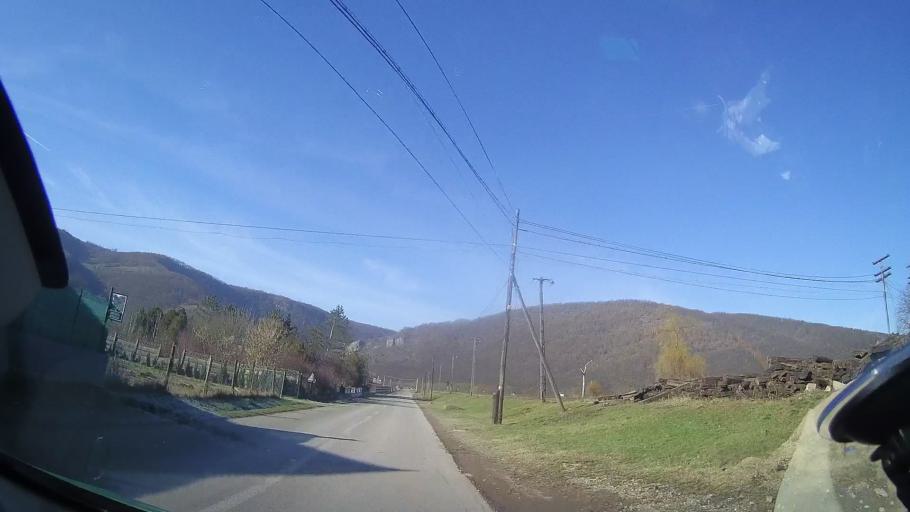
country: RO
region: Bihor
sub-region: Comuna Suncuius
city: Suncuius
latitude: 46.9487
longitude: 22.5362
